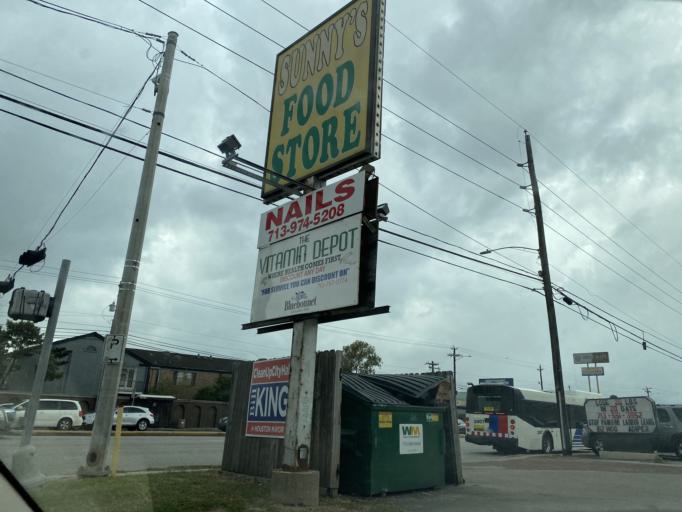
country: US
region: Texas
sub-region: Harris County
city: Hunters Creek Village
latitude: 29.7380
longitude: -95.4929
